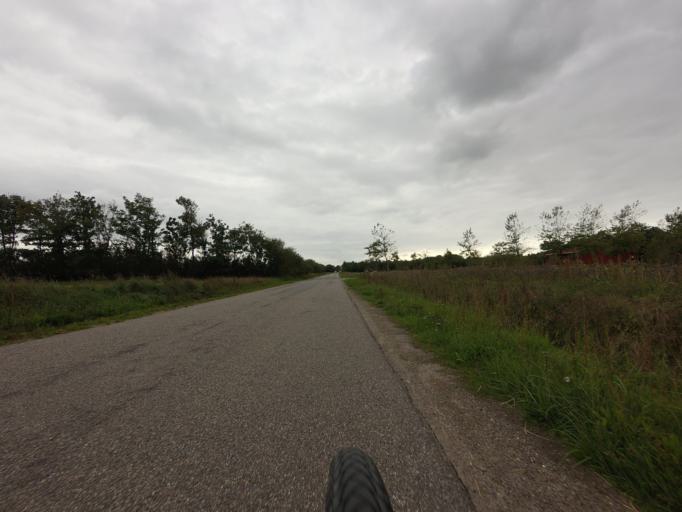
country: DK
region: North Denmark
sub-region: Hjorring Kommune
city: Hirtshals
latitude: 57.5676
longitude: 10.0327
